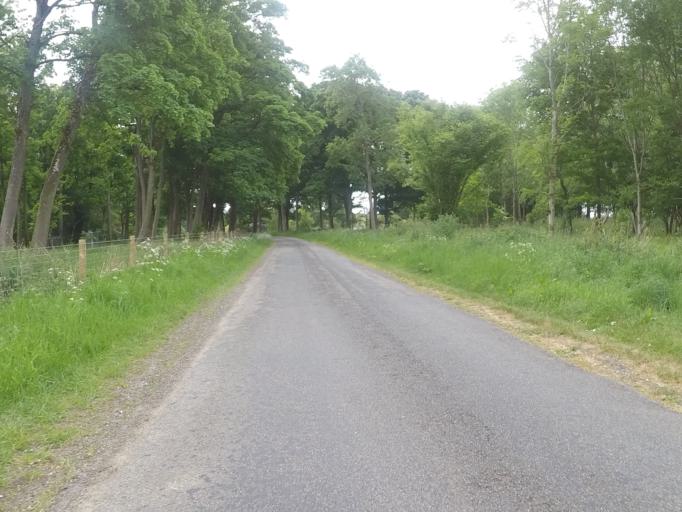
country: GB
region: England
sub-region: Oxfordshire
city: Charlbury
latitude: 51.8711
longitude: -1.5133
